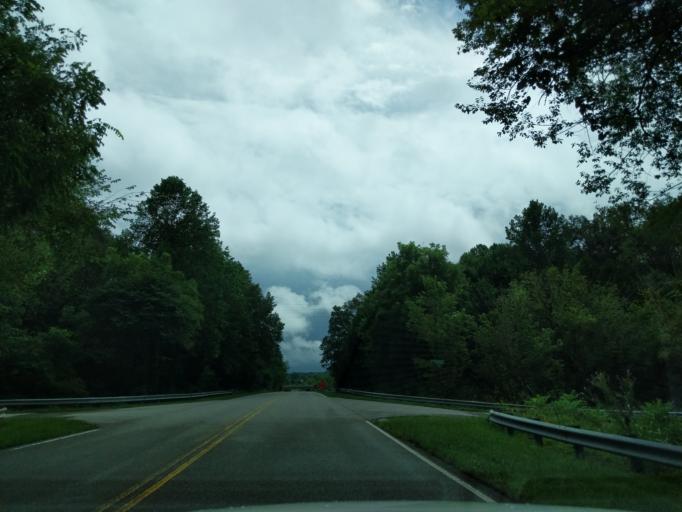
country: US
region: Kentucky
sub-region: Barren County
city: Cave City
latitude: 37.1018
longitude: -86.0569
